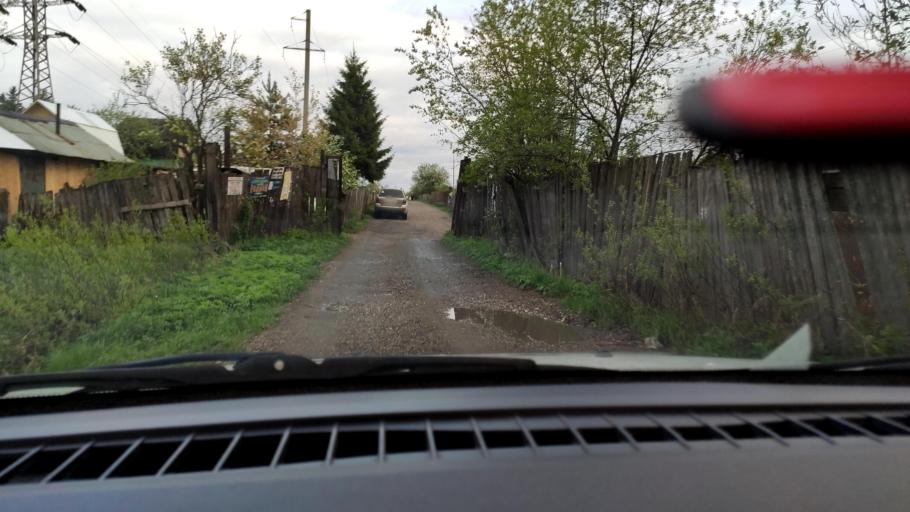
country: RU
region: Perm
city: Polazna
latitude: 58.1336
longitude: 56.4101
